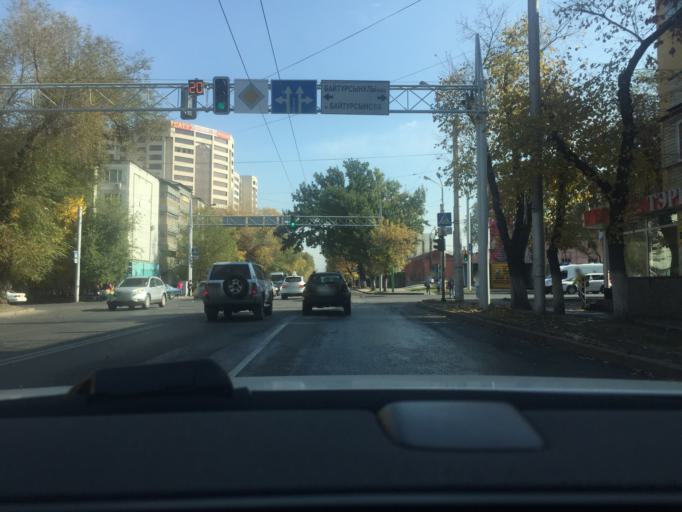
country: KZ
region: Almaty Qalasy
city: Almaty
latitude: 43.2585
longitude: 76.9245
